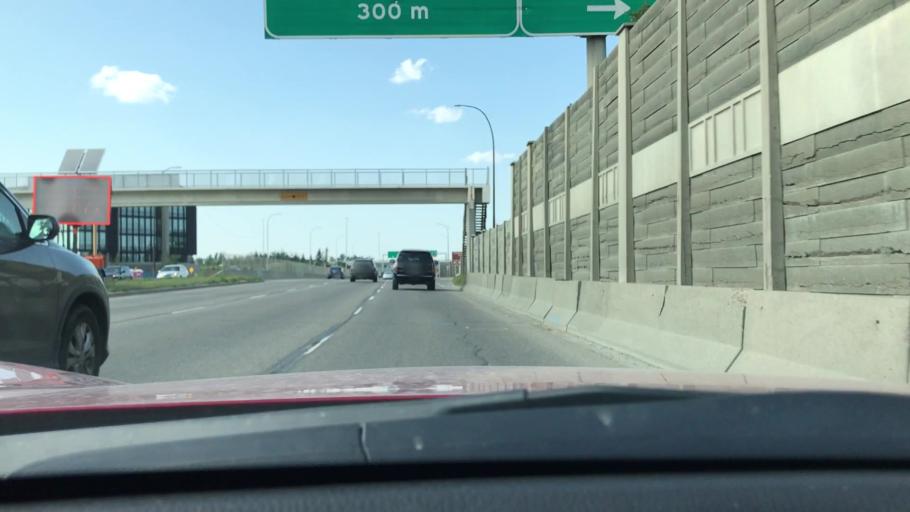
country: CA
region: Alberta
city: Calgary
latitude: 51.0039
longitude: -114.1178
